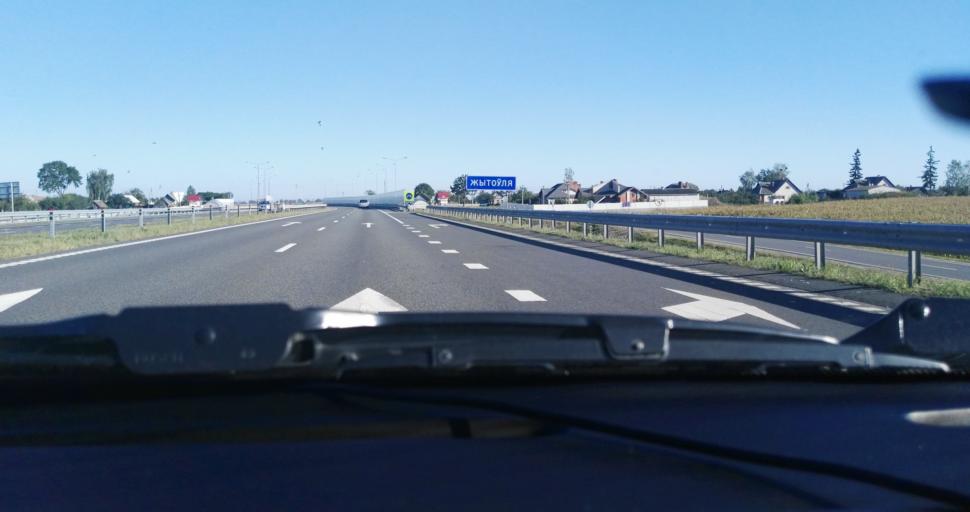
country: BY
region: Gomel
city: Buda-Kashalyova
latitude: 52.5168
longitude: 30.6283
